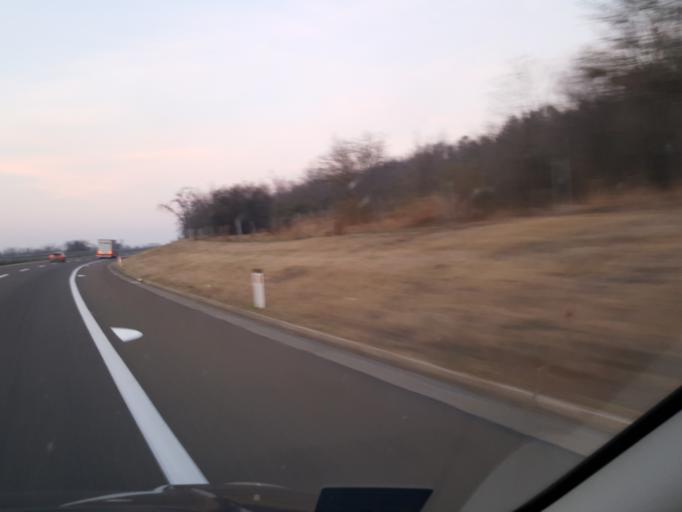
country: RS
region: Central Serbia
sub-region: Rasinski Okrug
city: Cicevac
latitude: 43.7679
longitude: 21.4356
